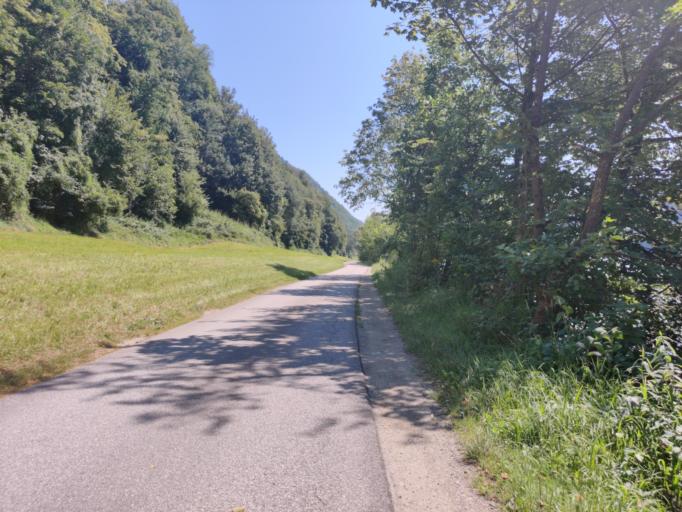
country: AT
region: Upper Austria
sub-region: Politischer Bezirk Rohrbach
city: Pfarrkirchen im Muehlkreis
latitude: 48.4587
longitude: 13.8166
